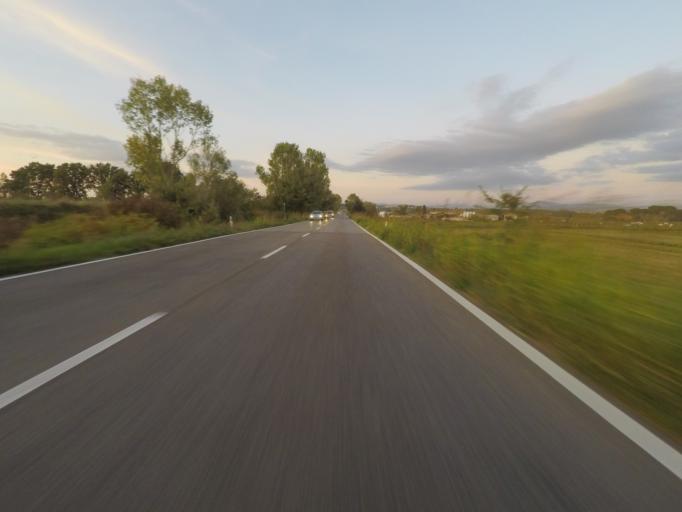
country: IT
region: Tuscany
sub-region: Provincia di Siena
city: Sinalunga
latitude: 43.1920
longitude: 11.7589
